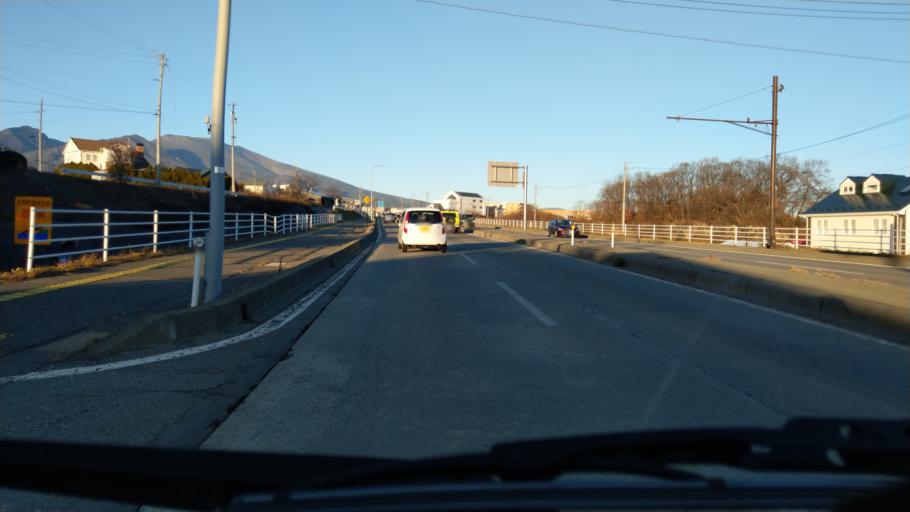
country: JP
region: Nagano
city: Komoro
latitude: 36.2820
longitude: 138.4717
